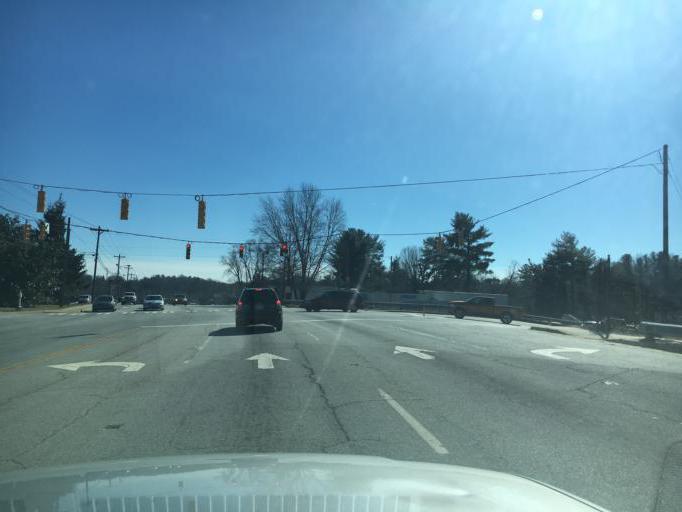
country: US
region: North Carolina
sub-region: Henderson County
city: Balfour
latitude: 35.3391
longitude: -82.4749
